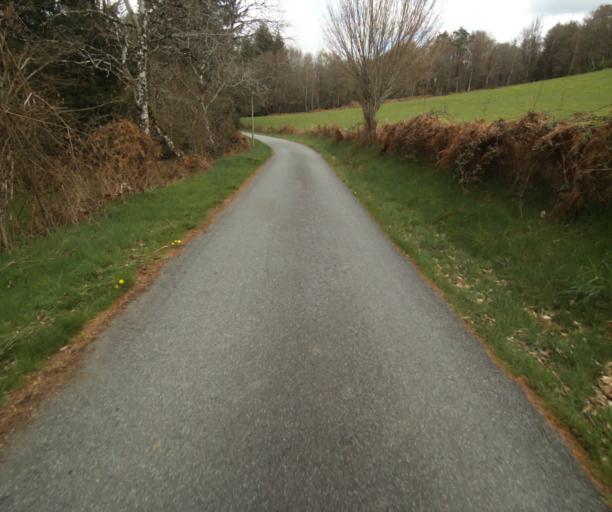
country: FR
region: Limousin
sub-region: Departement de la Correze
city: Egletons
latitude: 45.3913
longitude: 1.9630
